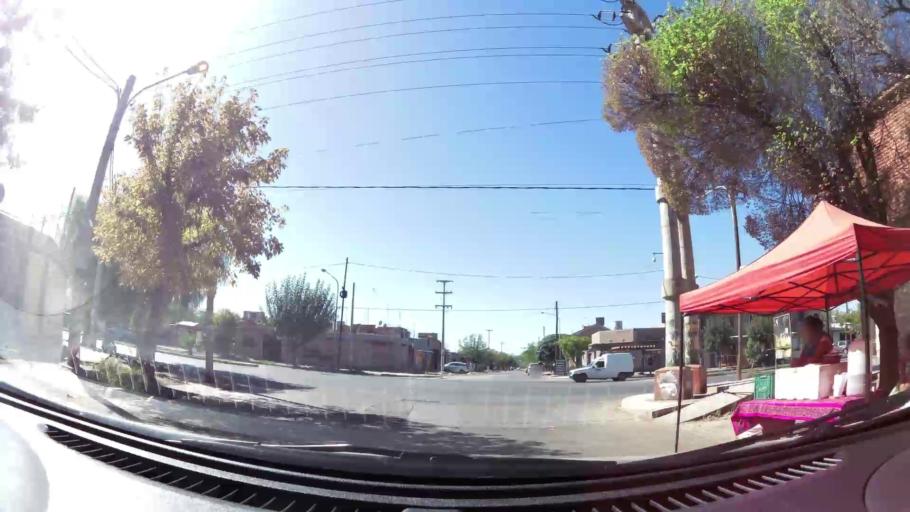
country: AR
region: Mendoza
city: Villa Nueva
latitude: -32.8812
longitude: -68.7985
